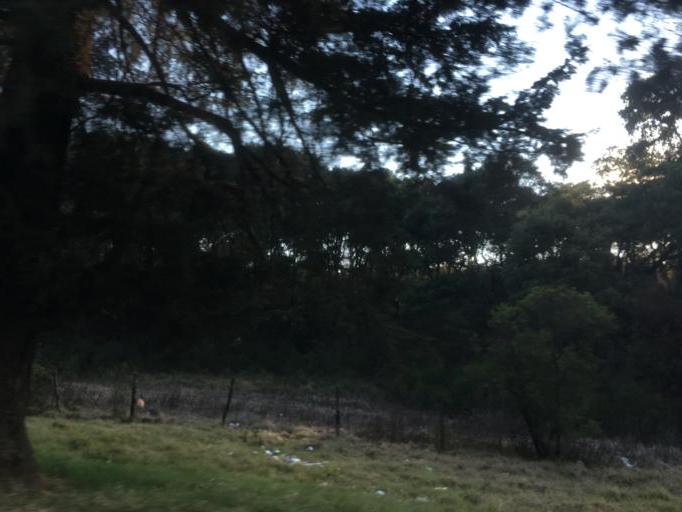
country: MX
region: Michoacan
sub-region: Morelia
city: Iratzio
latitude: 19.6251
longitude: -101.4633
